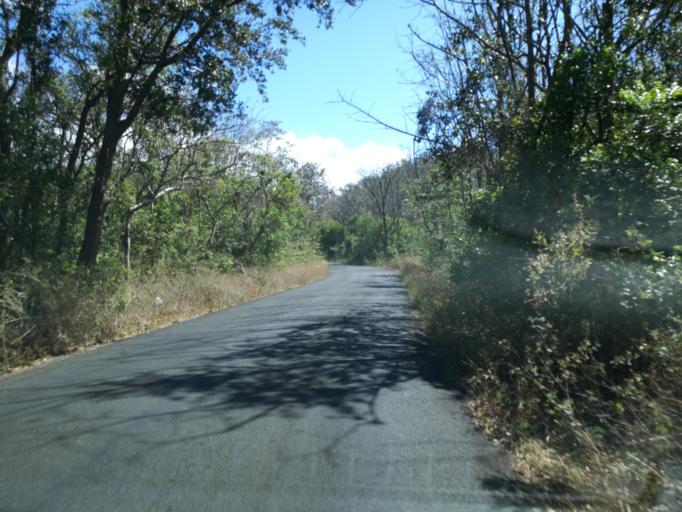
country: CR
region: Guanacaste
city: Liberia
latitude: 10.7497
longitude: -85.3732
